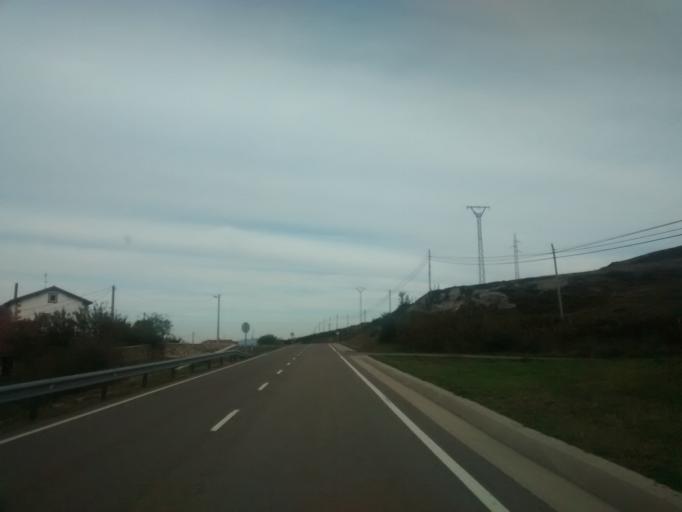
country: ES
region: Castille and Leon
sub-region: Provincia de Burgos
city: Arija
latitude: 42.9750
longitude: -4.0014
